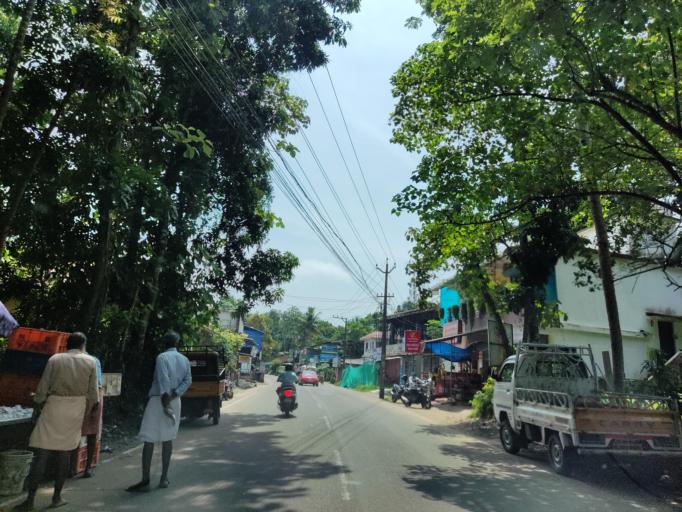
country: IN
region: Kerala
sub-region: Alappuzha
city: Chengannur
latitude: 9.3096
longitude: 76.5666
